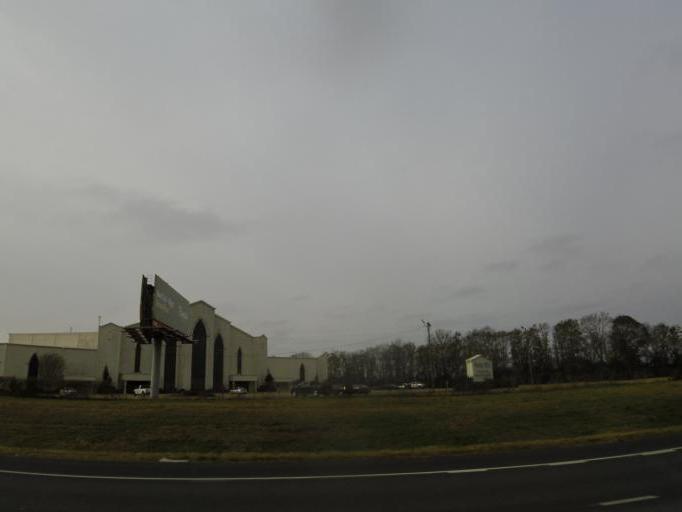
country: US
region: Alabama
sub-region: Elmore County
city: Millbrook
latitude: 32.4835
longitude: -86.4052
